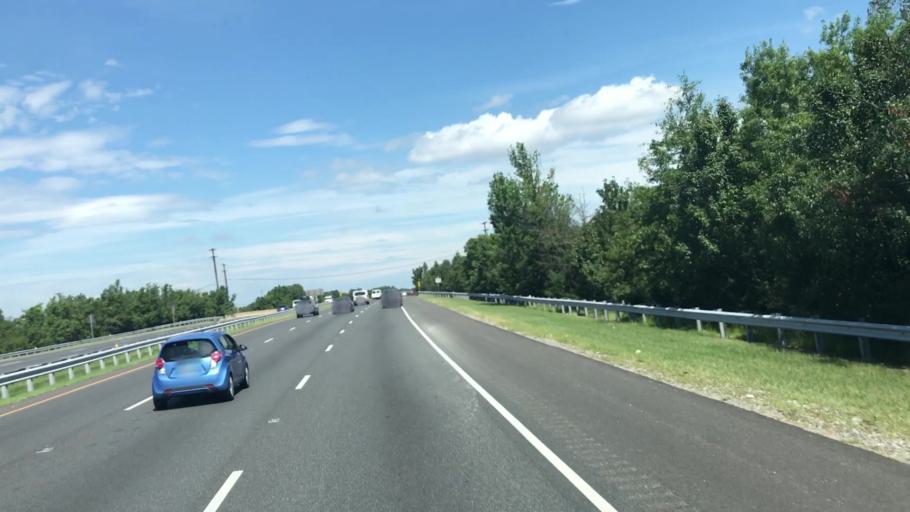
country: US
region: Maryland
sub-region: Prince George's County
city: Clinton
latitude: 38.7666
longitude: -76.8839
